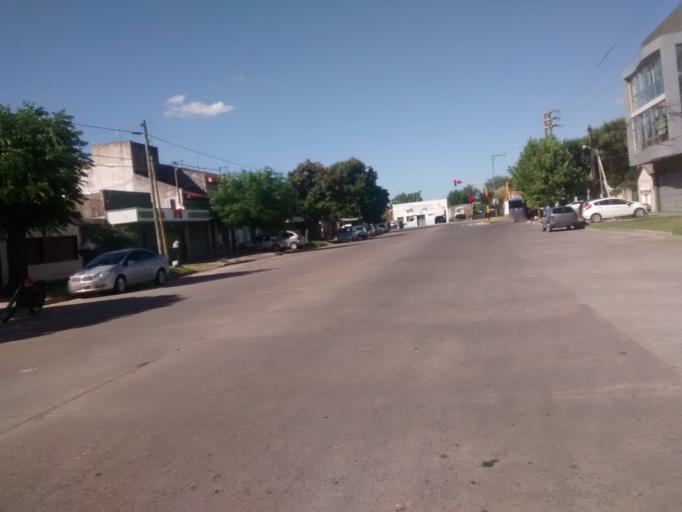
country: AR
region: Buenos Aires
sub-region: Partido de La Plata
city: La Plata
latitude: -34.9246
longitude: -57.9056
